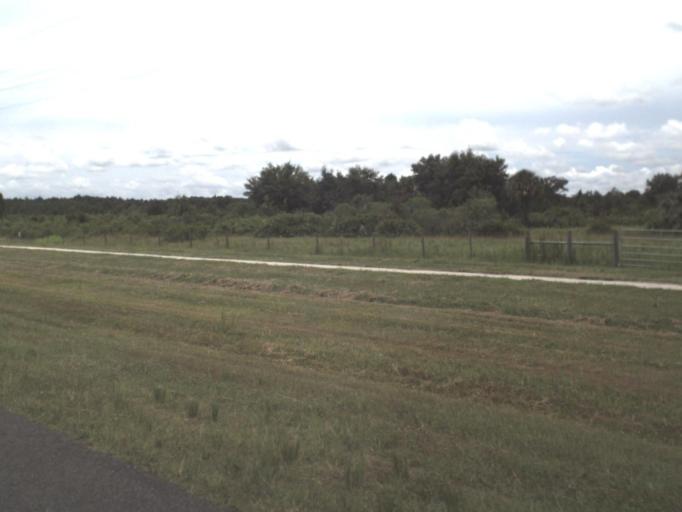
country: US
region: Florida
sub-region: Pasco County
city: Wesley Chapel
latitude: 28.1947
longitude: -82.3343
